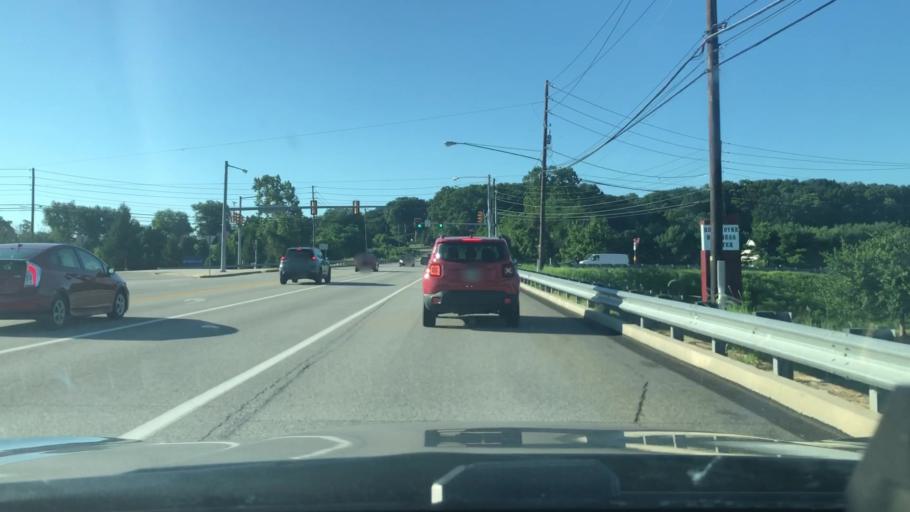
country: US
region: Pennsylvania
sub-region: Cumberland County
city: Shiremanstown
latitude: 40.2056
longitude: -76.9552
